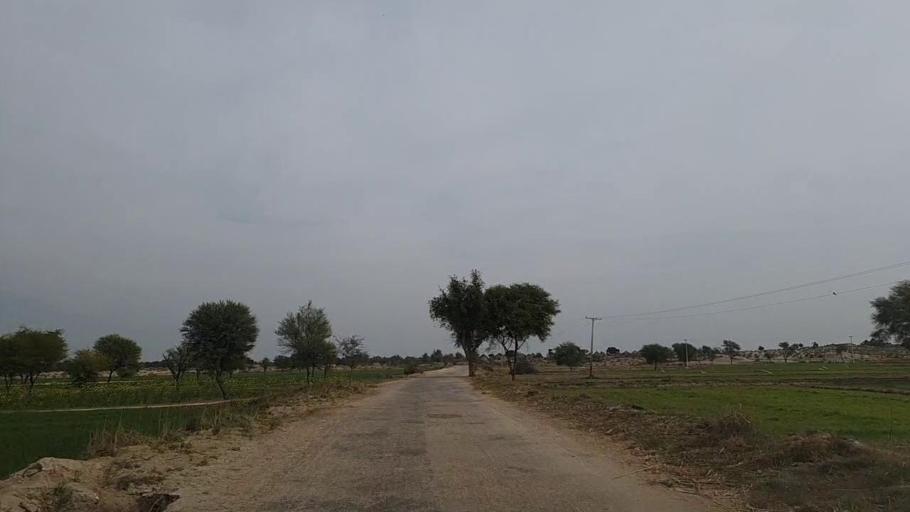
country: PK
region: Sindh
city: Jam Sahib
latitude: 26.4002
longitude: 68.5167
